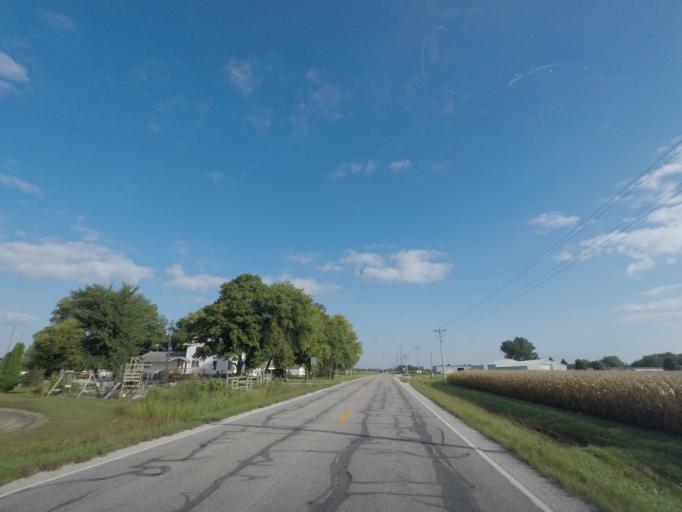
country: US
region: Iowa
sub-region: Story County
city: Nevada
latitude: 42.0000
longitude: -93.4628
